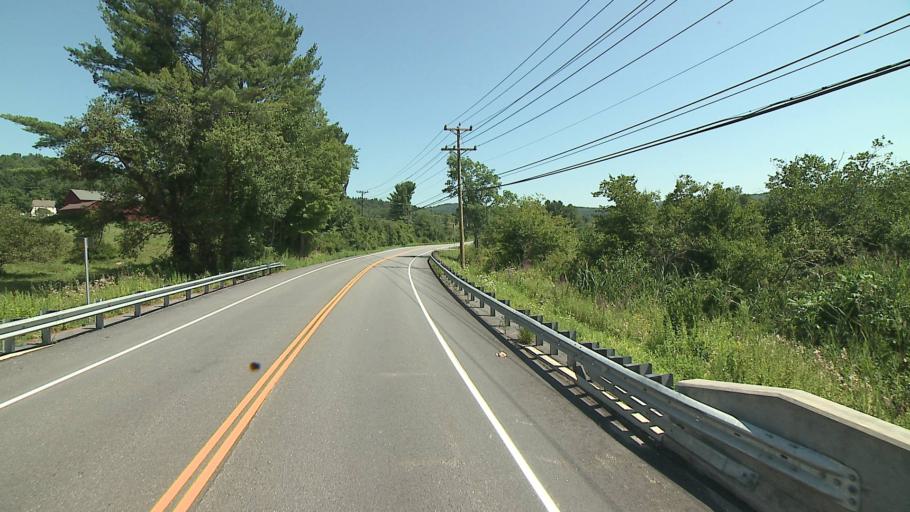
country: US
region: Connecticut
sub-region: Litchfield County
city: New Preston
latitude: 41.8409
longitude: -73.3488
